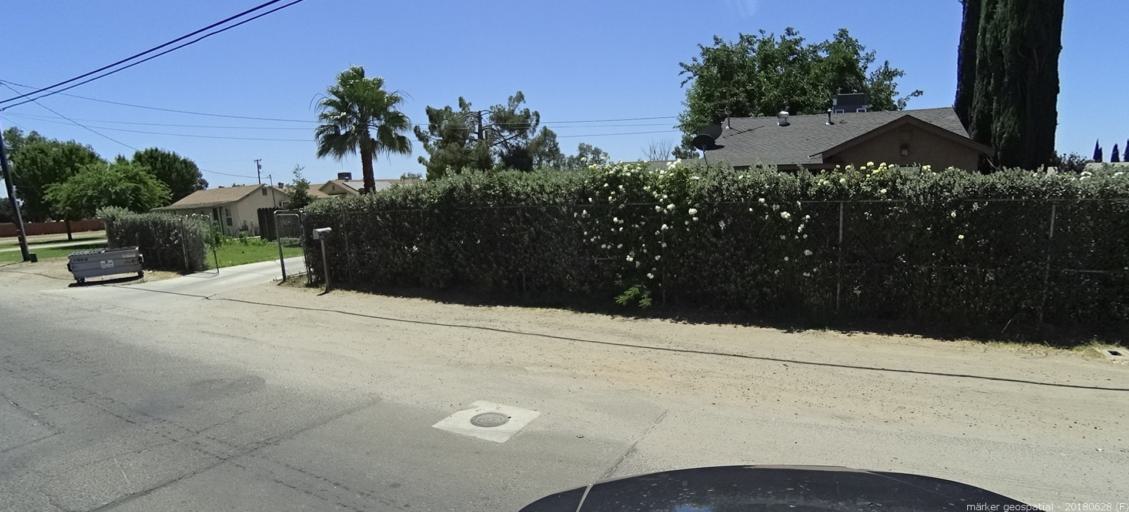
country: US
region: California
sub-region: Madera County
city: Parksdale
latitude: 36.9454
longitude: -120.0222
